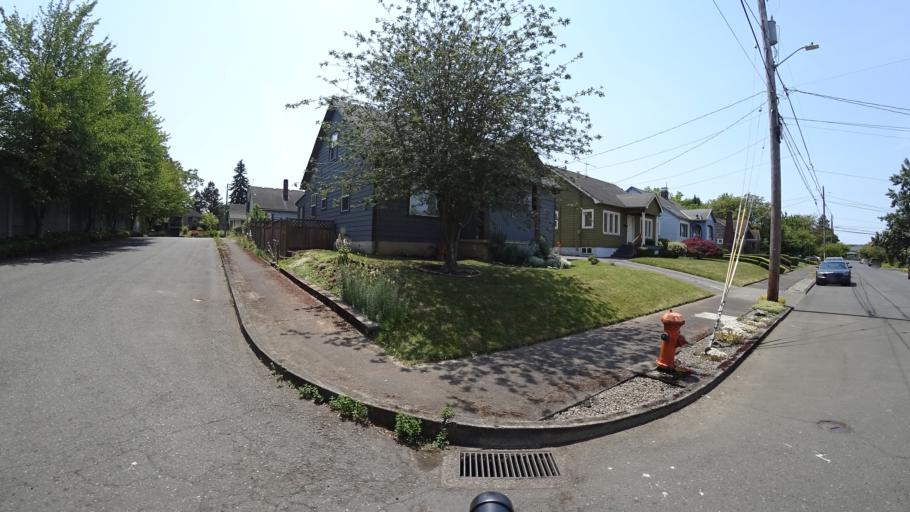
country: US
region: Oregon
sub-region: Multnomah County
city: Portland
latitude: 45.5793
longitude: -122.6791
